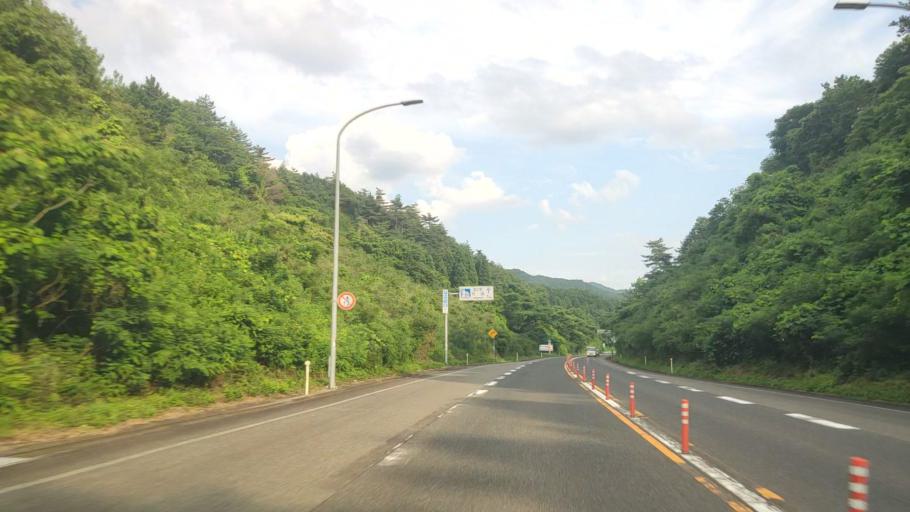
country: JP
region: Tottori
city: Kurayoshi
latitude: 35.3383
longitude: 133.7526
